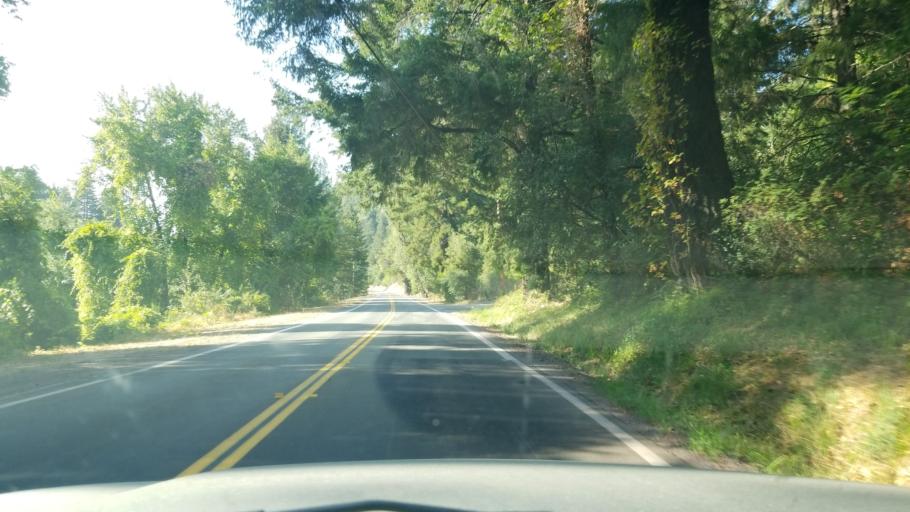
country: US
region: California
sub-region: Humboldt County
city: Redway
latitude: 40.1989
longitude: -123.7748
